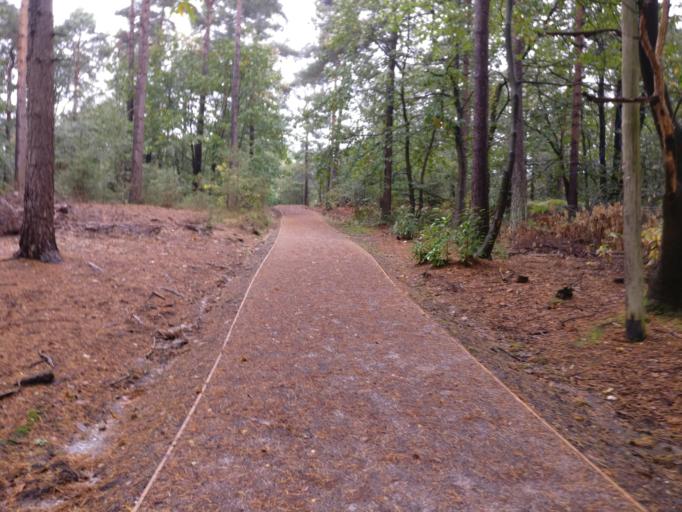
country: GB
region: England
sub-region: Surrey
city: Frimley
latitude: 51.3160
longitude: -0.7080
